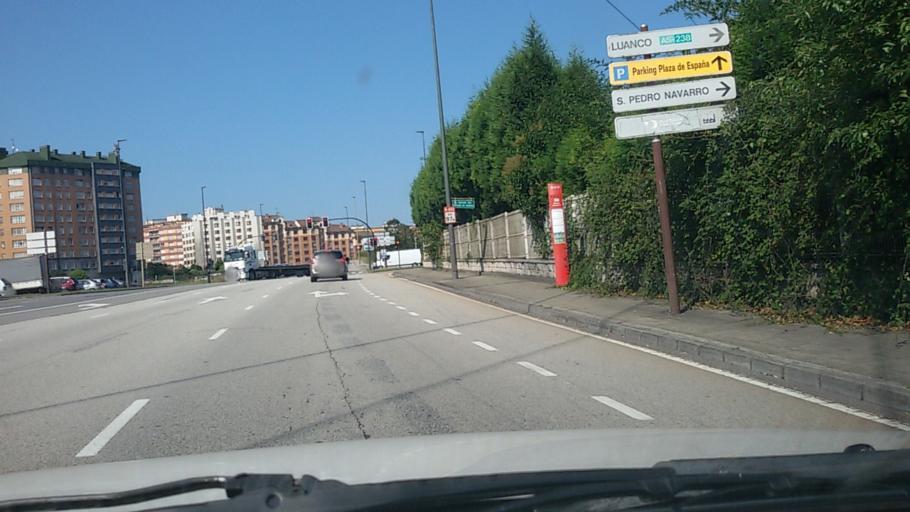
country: ES
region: Asturias
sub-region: Province of Asturias
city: Aviles
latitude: 43.5517
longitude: -5.9131
